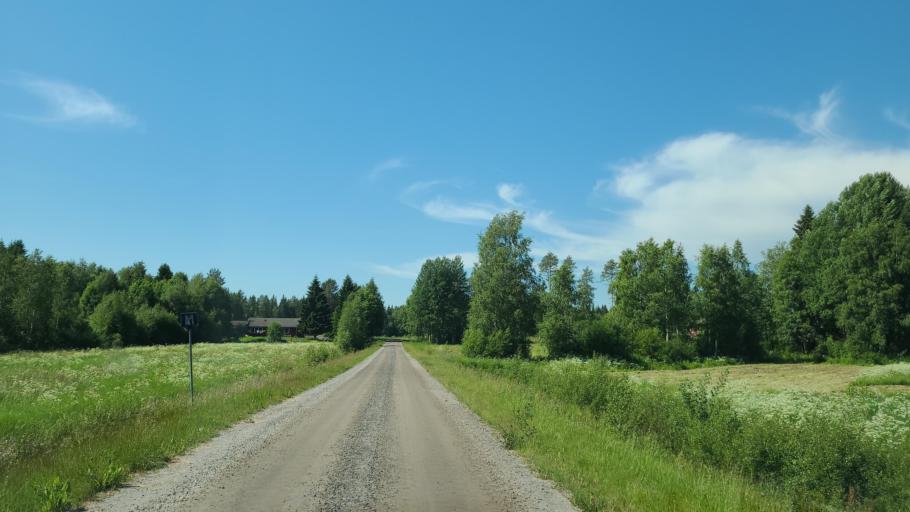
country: SE
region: Vaesterbotten
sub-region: Robertsfors Kommun
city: Robertsfors
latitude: 64.0877
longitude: 20.8453
